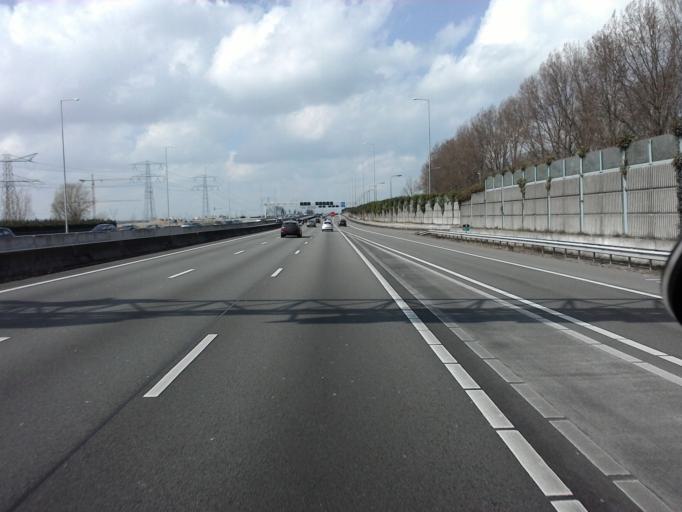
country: NL
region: North Holland
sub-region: Gemeente Weesp
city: Weesp
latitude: 52.3242
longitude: 5.0737
